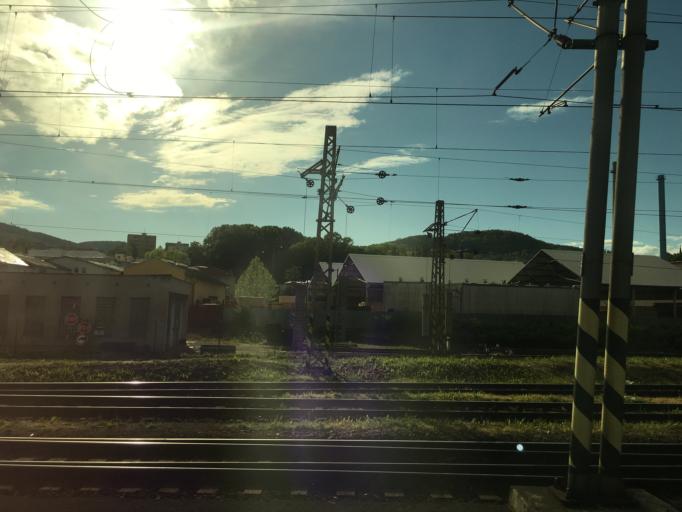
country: CZ
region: Ustecky
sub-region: Okres Decin
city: Decin
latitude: 50.7605
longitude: 14.1958
